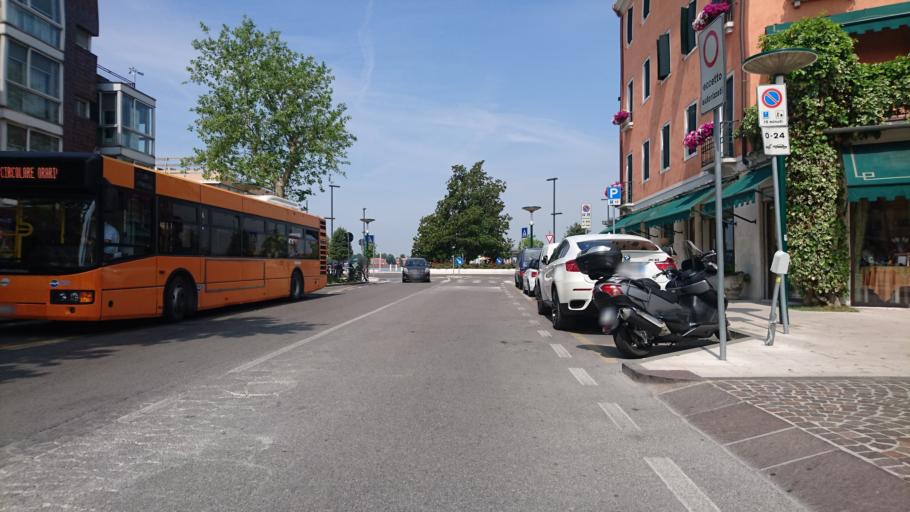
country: IT
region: Veneto
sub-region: Provincia di Venezia
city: Lido
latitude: 45.4168
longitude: 12.3690
